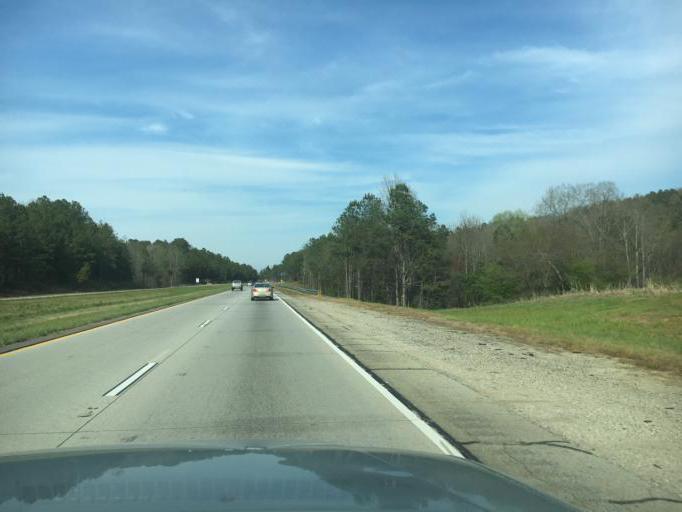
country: US
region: Georgia
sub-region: Hall County
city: Lula
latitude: 34.3602
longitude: -83.7458
